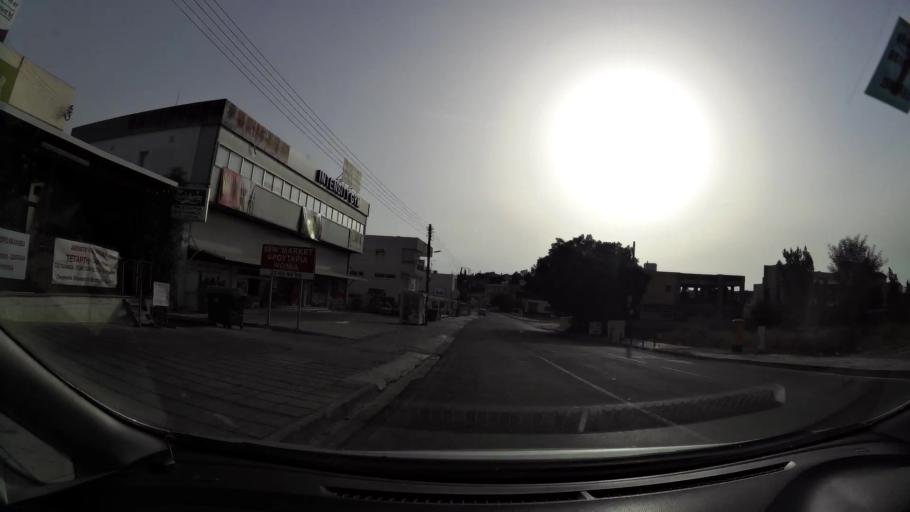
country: CY
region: Lefkosia
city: Geri
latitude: 35.0649
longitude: 33.3862
